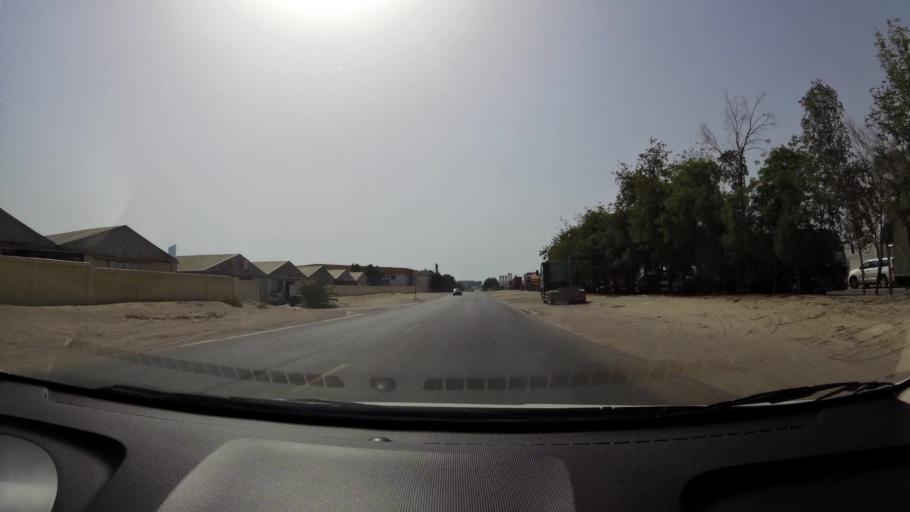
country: AE
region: Ash Shariqah
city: Sharjah
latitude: 25.2316
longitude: 55.3698
